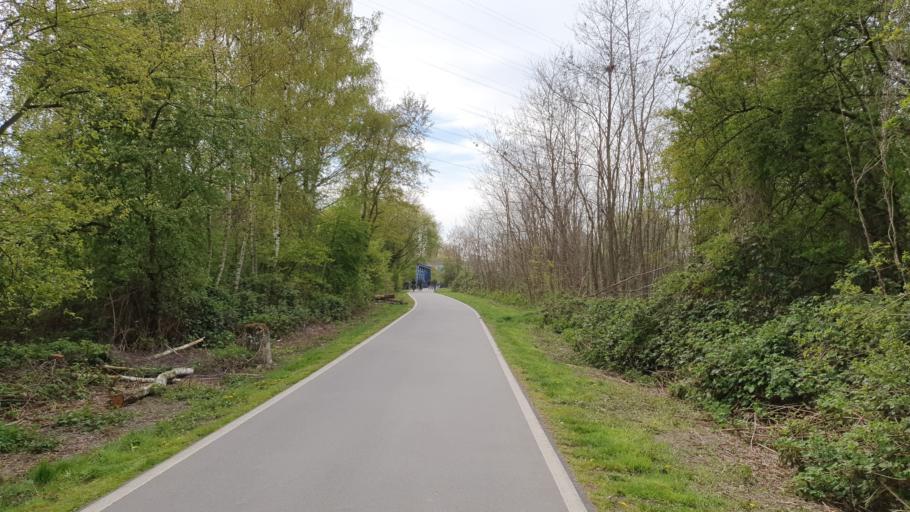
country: DE
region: North Rhine-Westphalia
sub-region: Regierungsbezirk Dusseldorf
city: Oberhausen
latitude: 51.4975
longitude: 6.8275
